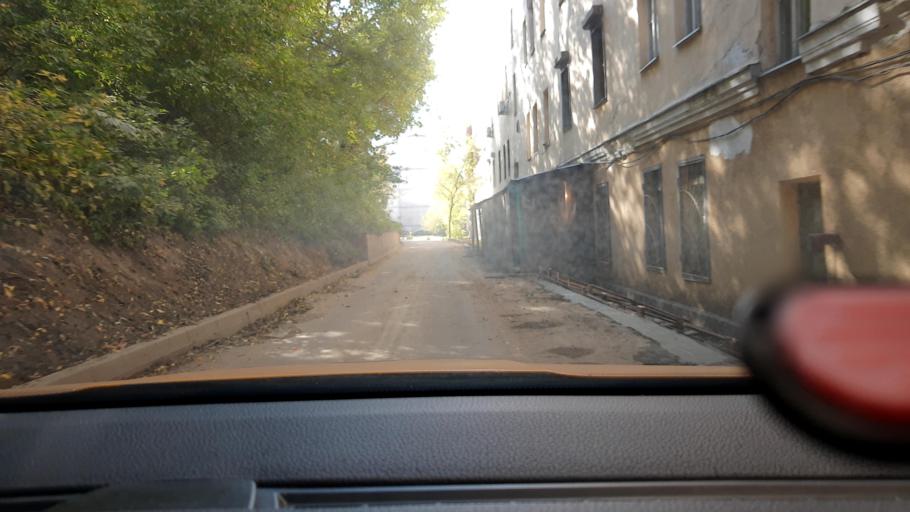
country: RU
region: Moscow
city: Strogino
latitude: 55.8403
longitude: 37.4138
